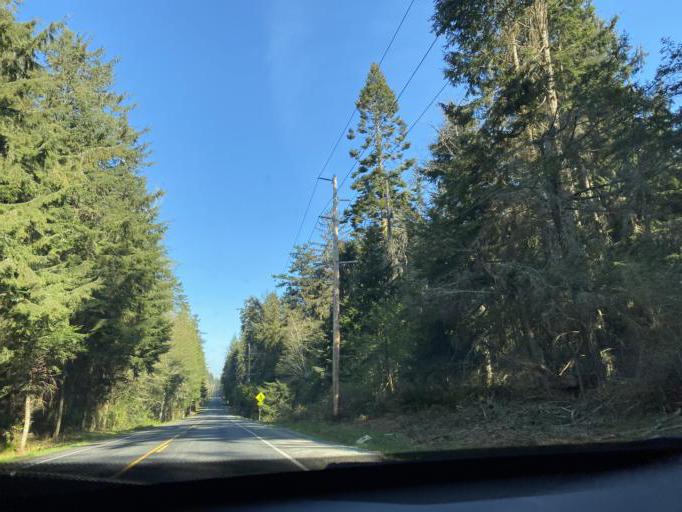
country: US
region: Washington
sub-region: Island County
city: Freeland
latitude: 48.0589
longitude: -122.5925
